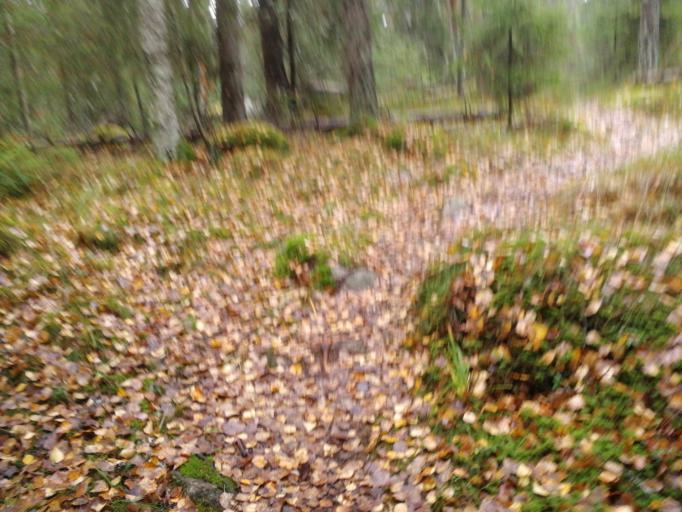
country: FI
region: Pirkanmaa
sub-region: Tampere
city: Tampere
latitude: 61.4565
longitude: 23.8798
